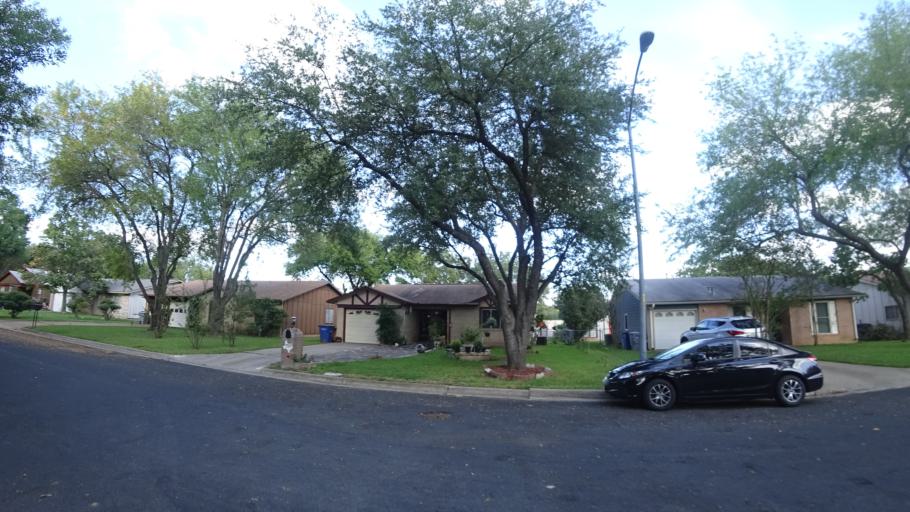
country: US
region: Texas
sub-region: Travis County
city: Onion Creek
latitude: 30.1908
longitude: -97.7924
